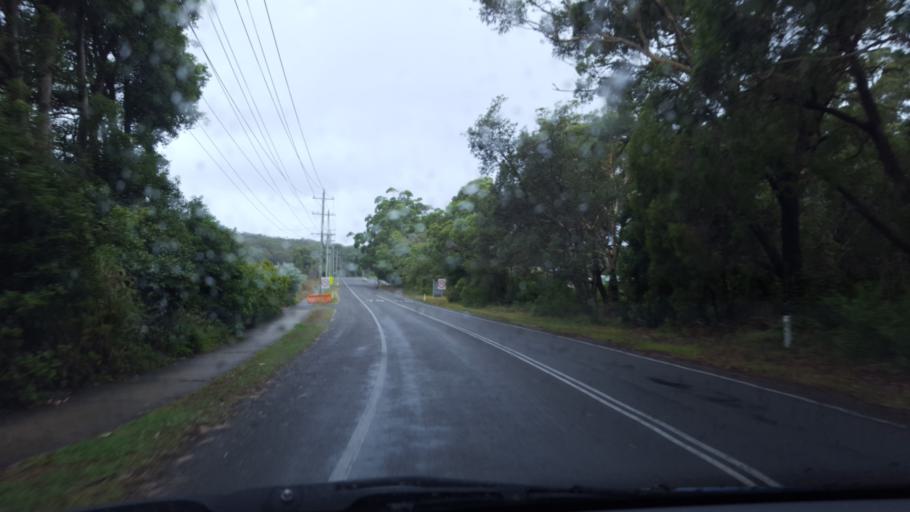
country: AU
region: New South Wales
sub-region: Port Stephens Shire
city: Anna Bay
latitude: -32.7763
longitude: 152.0949
